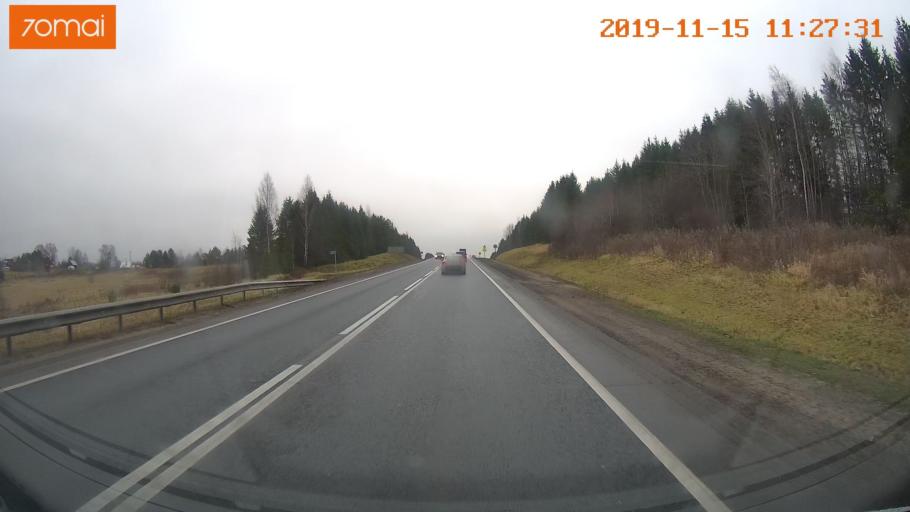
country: RU
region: Vologda
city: Molochnoye
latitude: 59.1700
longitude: 39.4686
